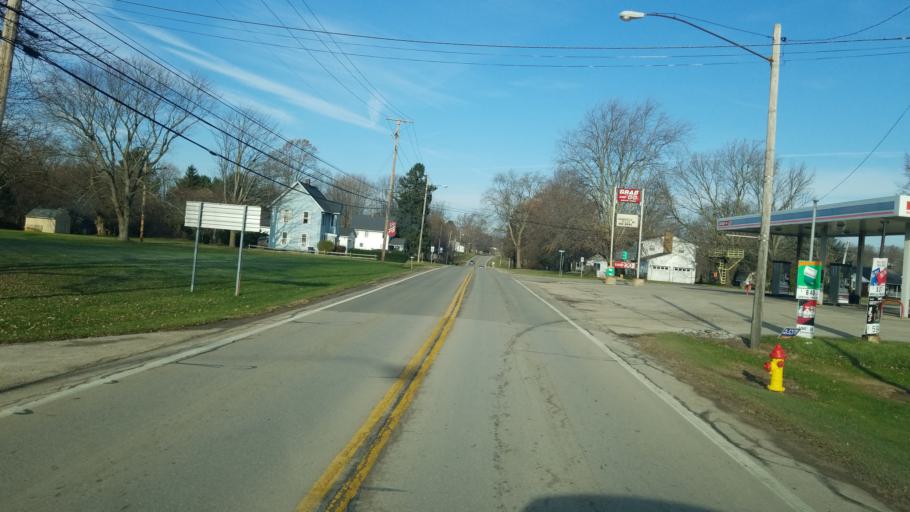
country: US
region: Ohio
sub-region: Ashtabula County
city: North Kingsville
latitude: 41.8834
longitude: -80.6678
